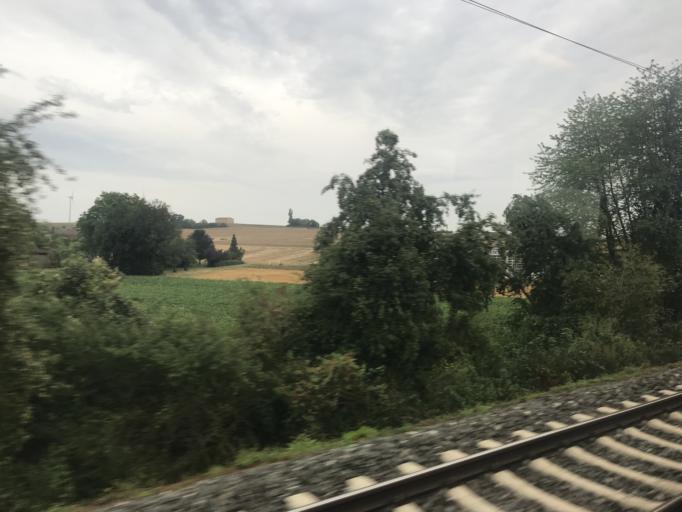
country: DE
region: Bavaria
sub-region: Regierungsbezirk Unterfranken
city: Werneck
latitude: 49.9453
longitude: 10.0868
